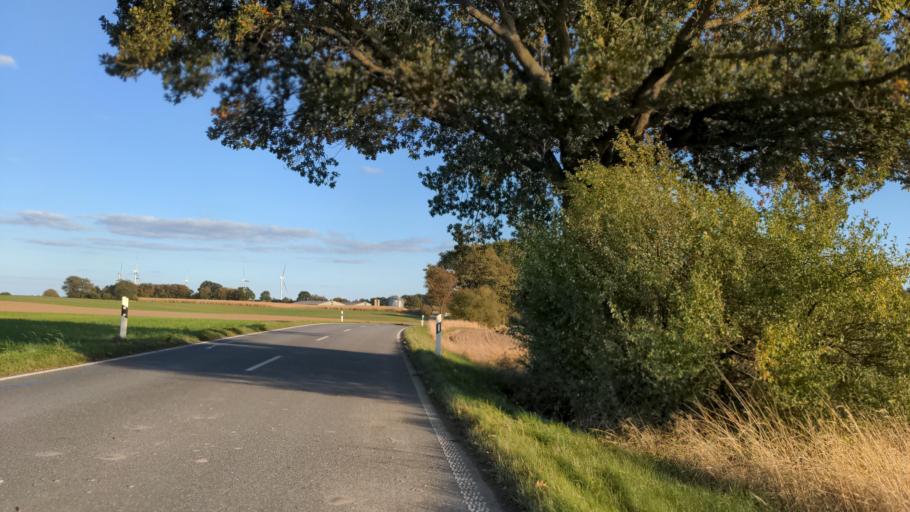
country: DE
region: Schleswig-Holstein
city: Pronstorf
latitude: 53.9626
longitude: 10.5131
